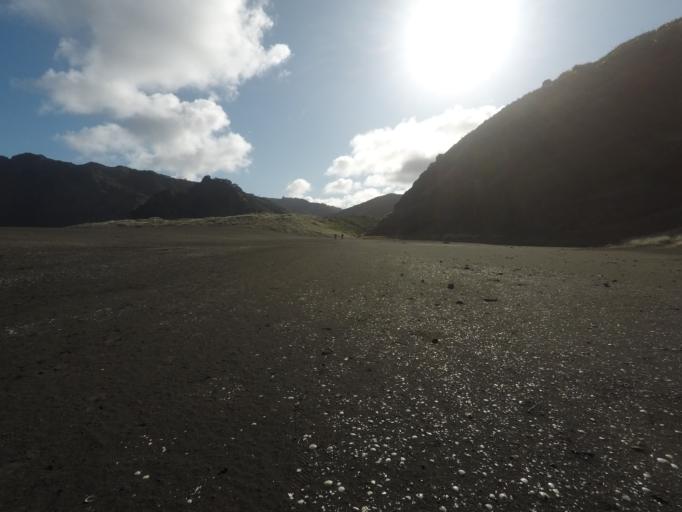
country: NZ
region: Auckland
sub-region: Auckland
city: Muriwai Beach
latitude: -36.9919
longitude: 174.4740
